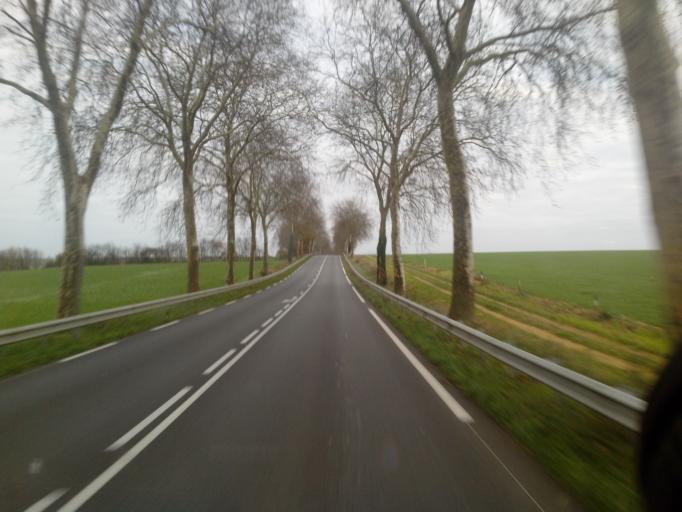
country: FR
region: Poitou-Charentes
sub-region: Departement de la Vienne
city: Ayron
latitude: 46.6602
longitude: 0.0417
